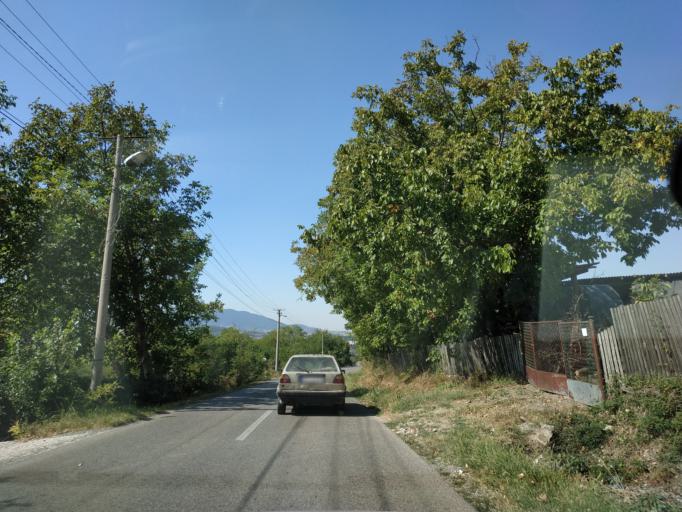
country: RS
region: Central Serbia
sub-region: Sumadijski Okrug
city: Topola
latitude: 44.2737
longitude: 20.6329
